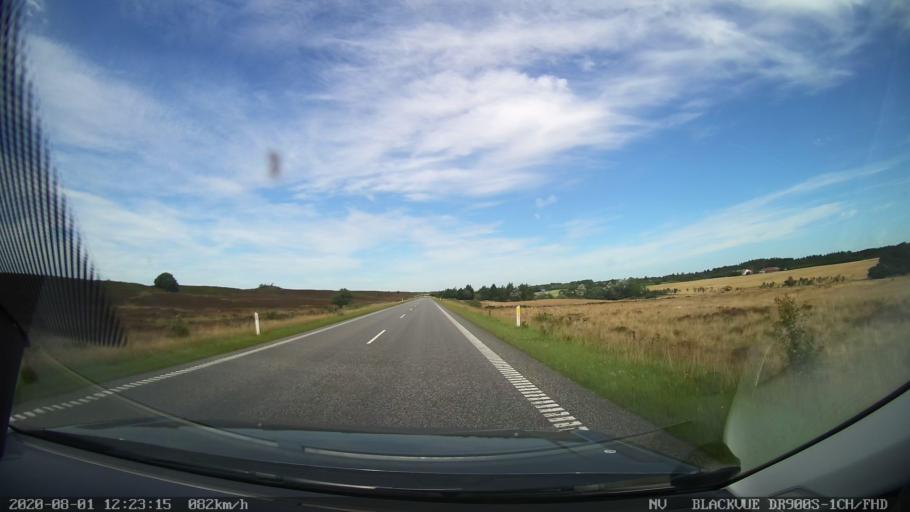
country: DK
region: Central Jutland
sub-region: Viborg Kommune
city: Stoholm
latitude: 56.3946
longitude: 9.1431
